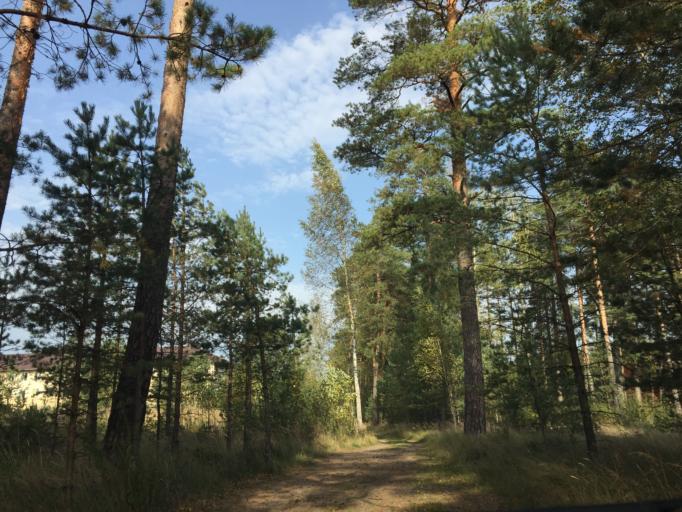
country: LV
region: Garkalne
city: Garkalne
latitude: 56.9587
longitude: 24.4258
